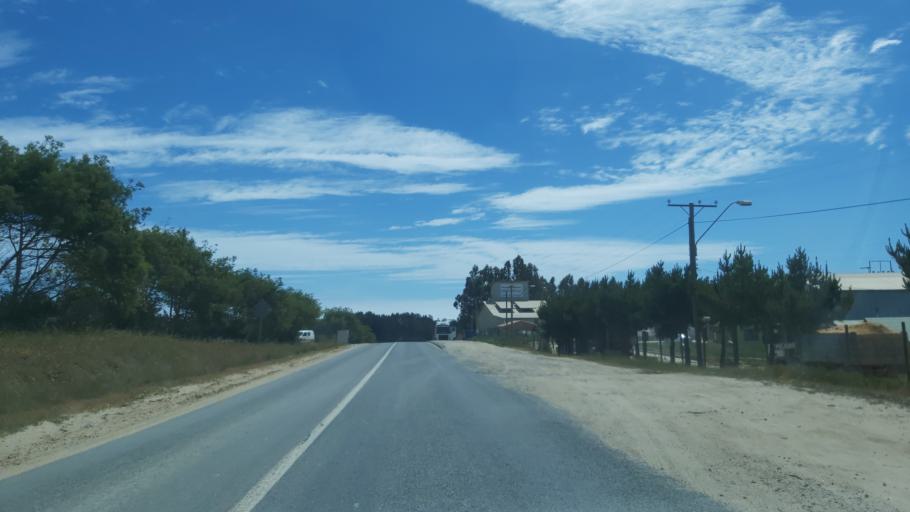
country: CL
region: Maule
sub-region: Provincia de Talca
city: Constitucion
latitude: -35.5652
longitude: -72.5958
